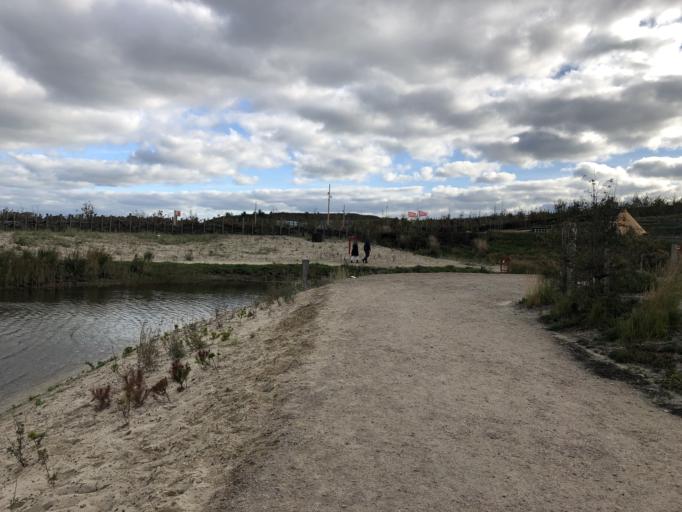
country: DK
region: Central Jutland
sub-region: Ringkobing-Skjern Kommune
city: Ringkobing
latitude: 56.1010
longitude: 8.2408
